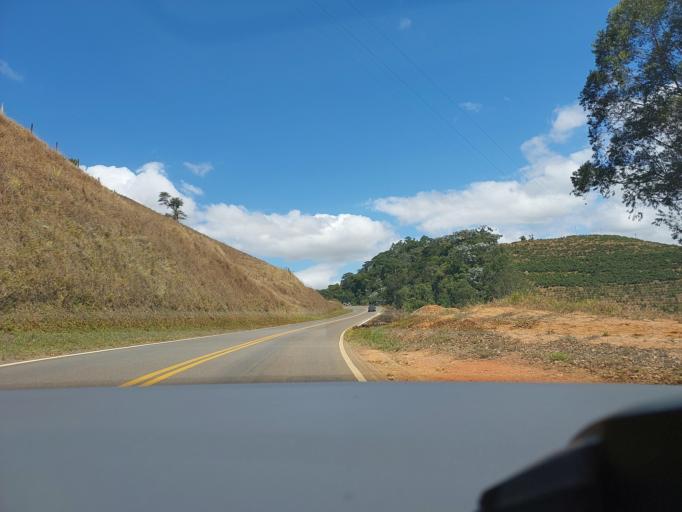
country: BR
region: Minas Gerais
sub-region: Mirai
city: Mirai
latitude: -21.0337
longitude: -42.5360
